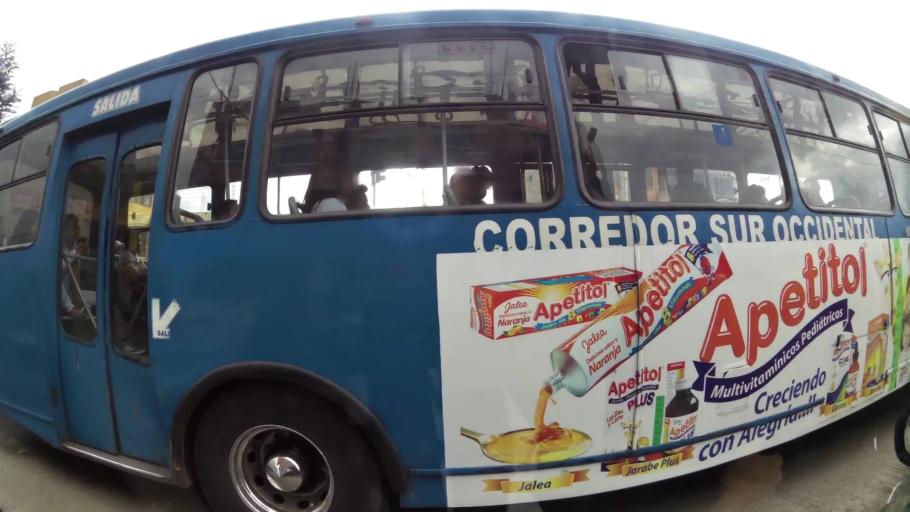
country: EC
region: Pichincha
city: Quito
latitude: -0.2584
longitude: -78.5446
